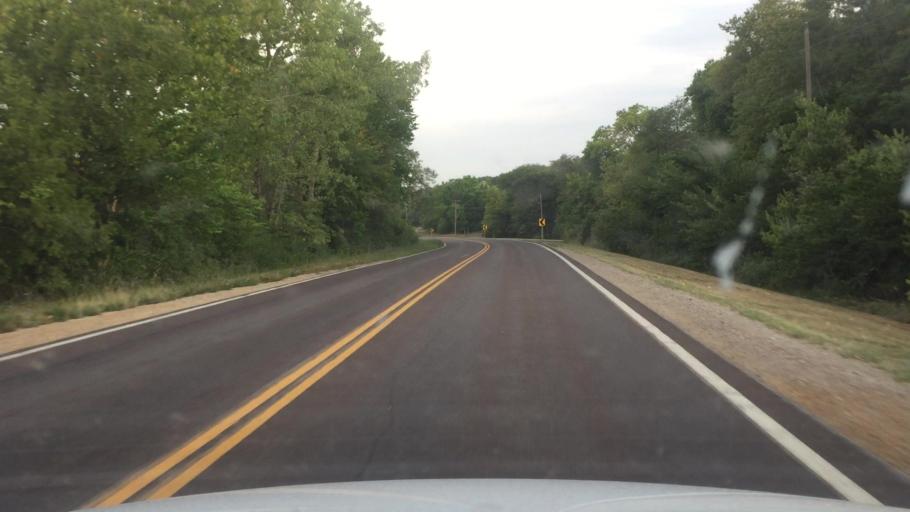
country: US
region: Kansas
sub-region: Shawnee County
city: Topeka
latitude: 39.0411
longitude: -95.5369
